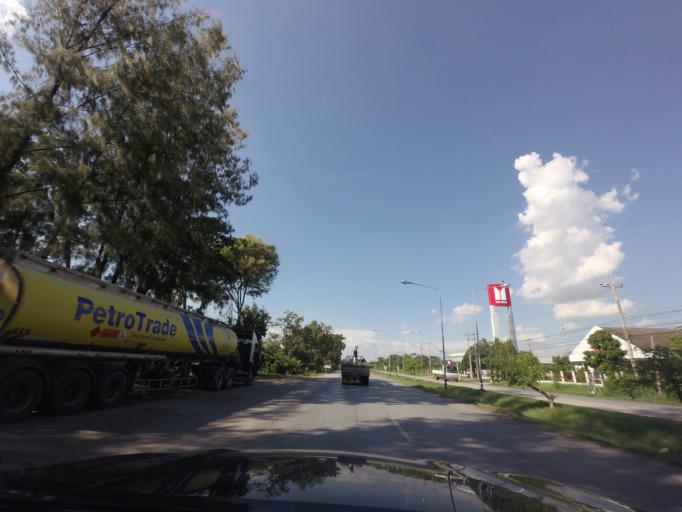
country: TH
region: Nakhon Ratchasima
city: Sida
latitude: 15.5385
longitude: 102.5458
